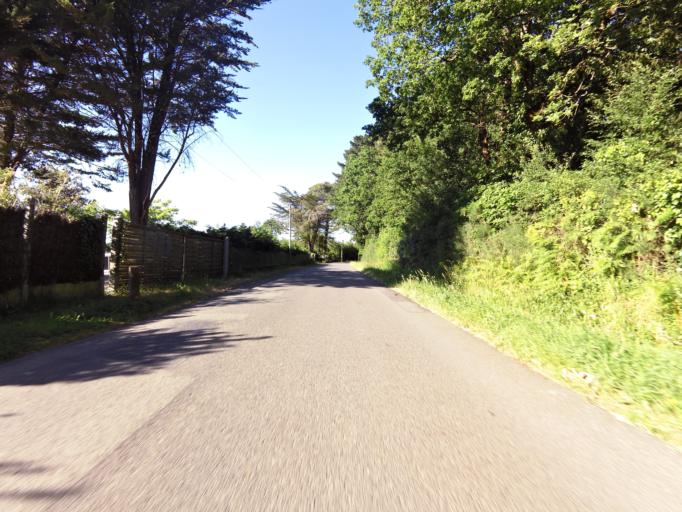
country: FR
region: Brittany
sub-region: Departement du Morbihan
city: Penestin
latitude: 47.4760
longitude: -2.4523
